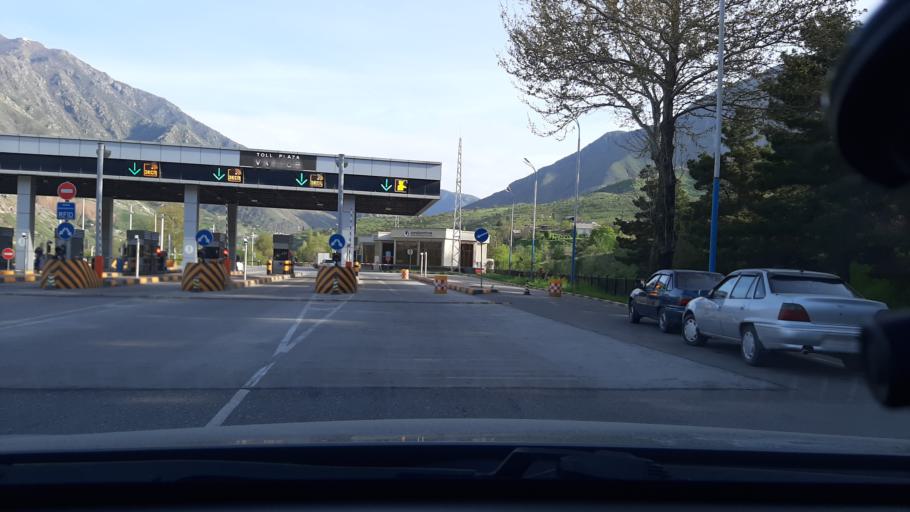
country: TJ
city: Varzob
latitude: 38.6828
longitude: 68.7916
